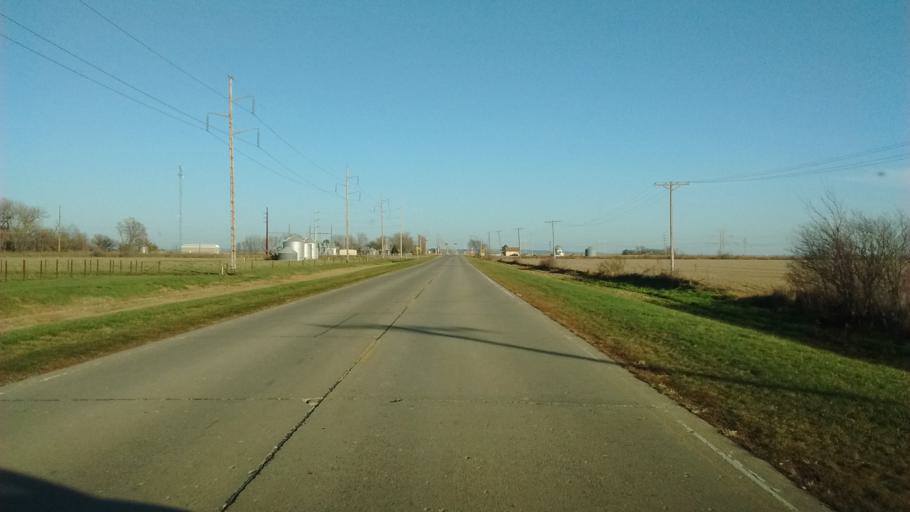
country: US
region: Iowa
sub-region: Woodbury County
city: Sergeant Bluff
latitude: 42.3302
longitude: -96.3070
